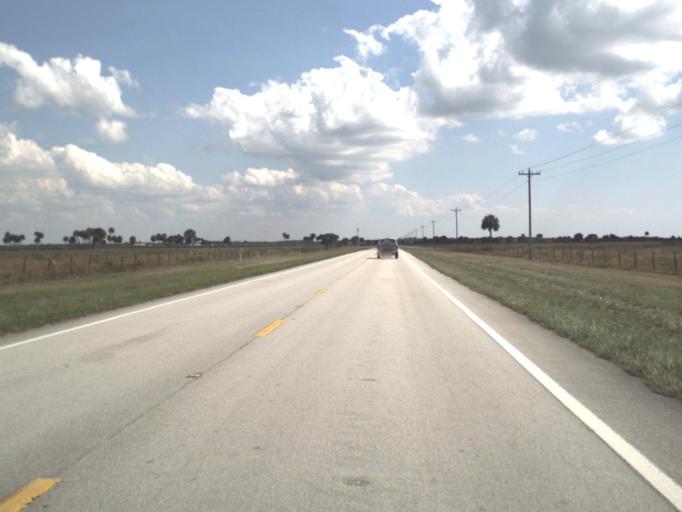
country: US
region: Florida
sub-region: Okeechobee County
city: Okeechobee
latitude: 27.3462
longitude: -80.9475
